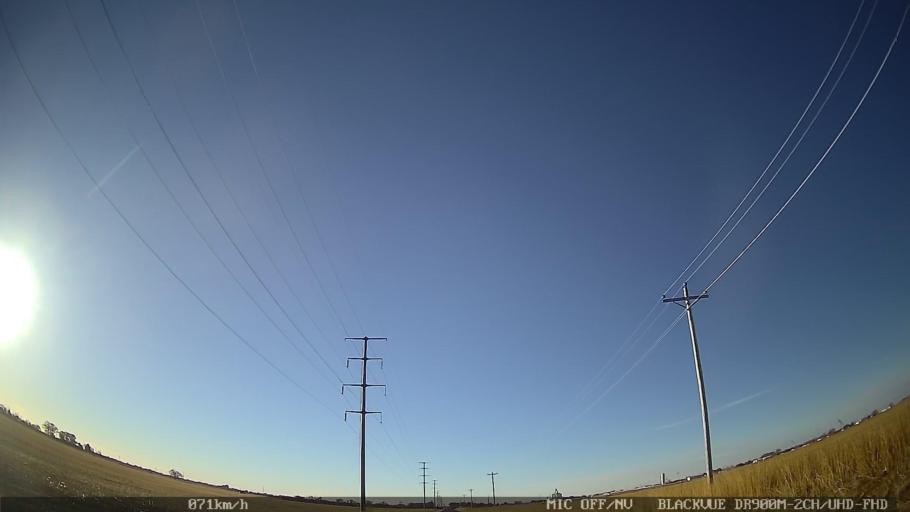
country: US
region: New Mexico
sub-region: Curry County
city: Clovis
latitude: 34.4224
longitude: -103.2493
